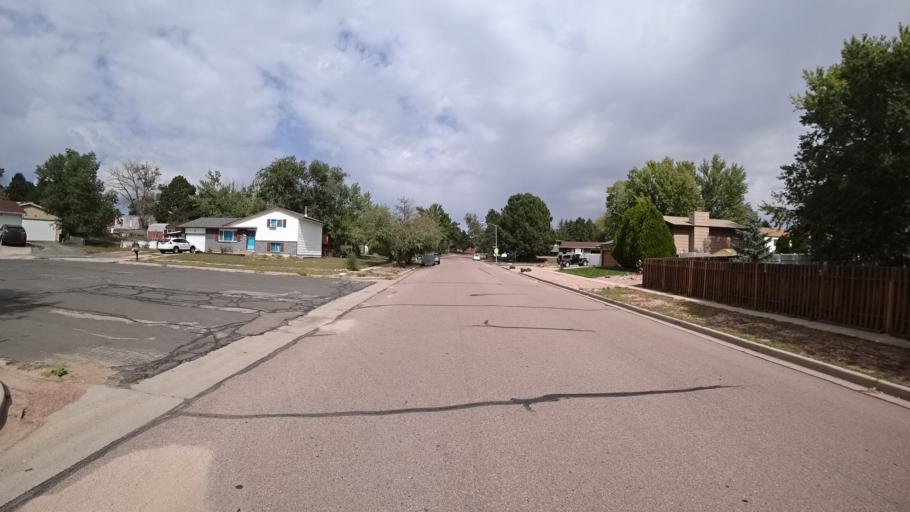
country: US
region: Colorado
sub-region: El Paso County
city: Cimarron Hills
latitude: 38.8491
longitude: -104.7323
